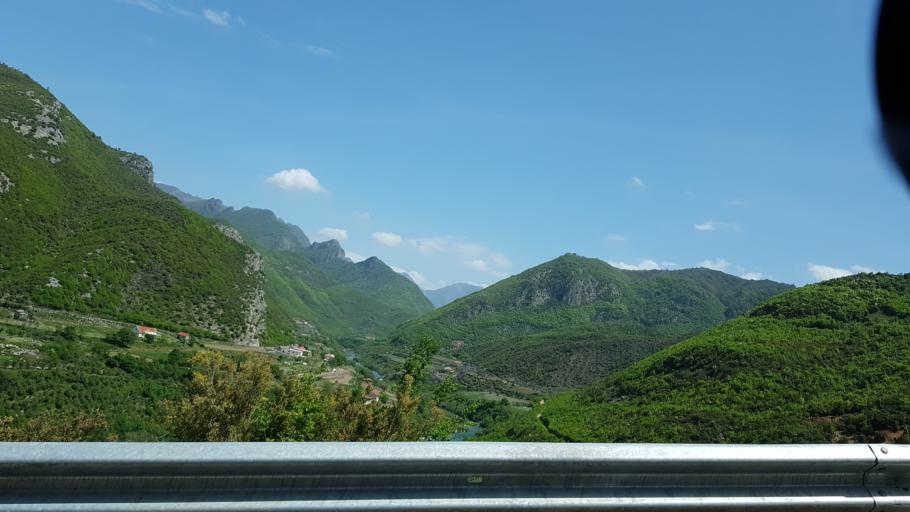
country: AL
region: Shkoder
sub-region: Rrethi i Shkodres
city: Guri i Zi
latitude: 42.1265
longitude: 19.6161
